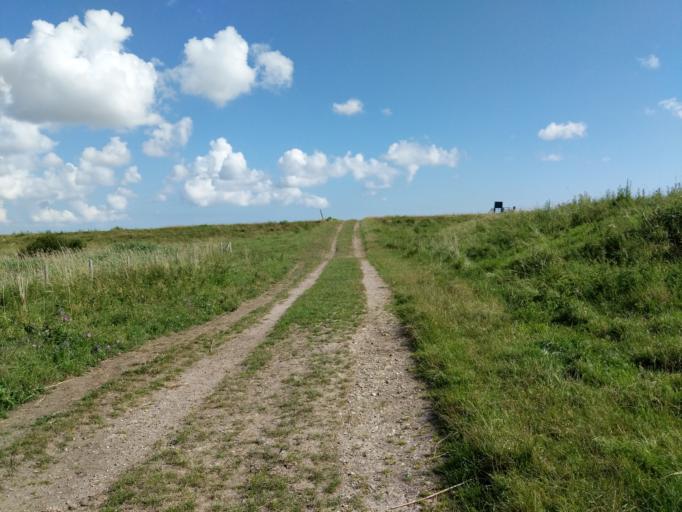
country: GB
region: England
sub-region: Kent
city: Dunkirk
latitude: 51.3432
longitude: 0.9574
